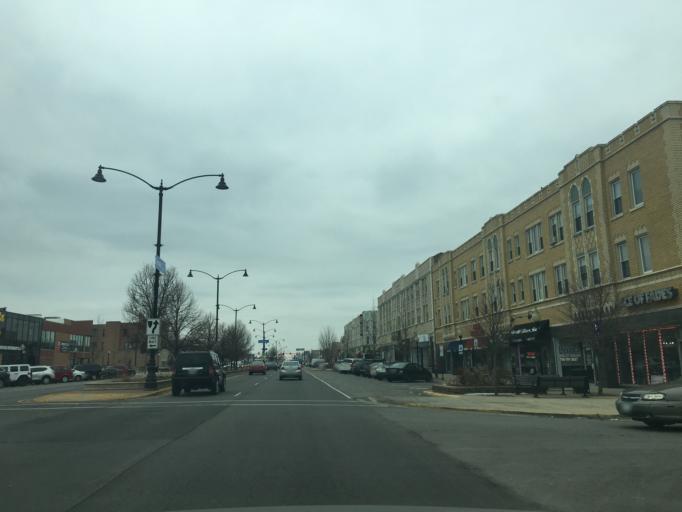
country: US
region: Illinois
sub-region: Cook County
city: Berwyn
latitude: 41.8508
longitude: -87.7846
